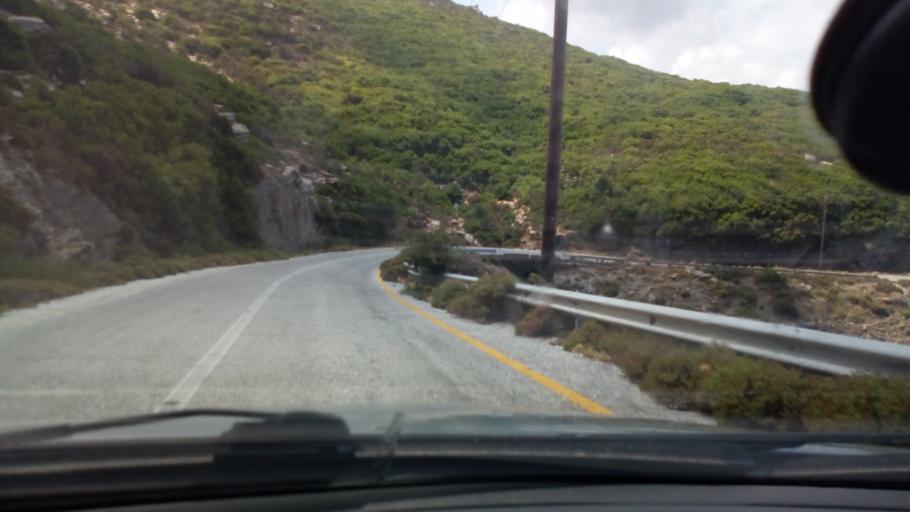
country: GR
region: North Aegean
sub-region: Nomos Samou
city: Agios Kirykos
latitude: 37.6512
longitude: 26.2841
